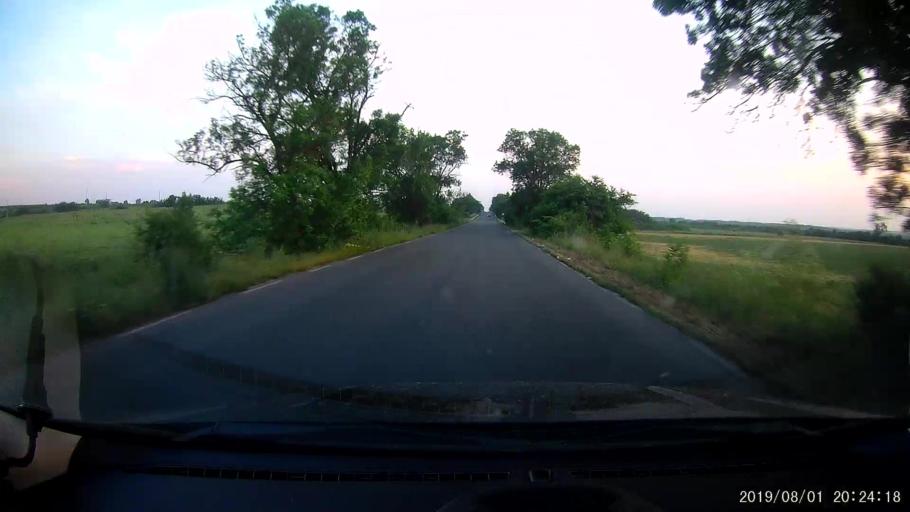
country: BG
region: Yambol
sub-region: Obshtina Elkhovo
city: Elkhovo
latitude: 42.2339
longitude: 26.5945
